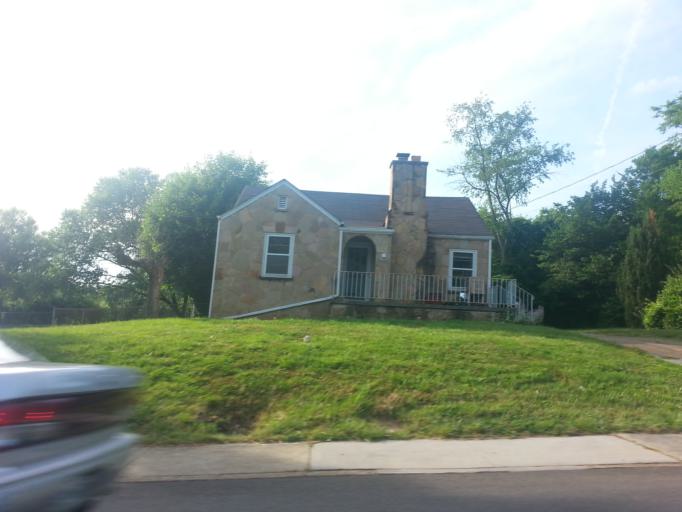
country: US
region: Tennessee
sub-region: Knox County
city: Knoxville
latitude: 35.9758
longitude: -83.8851
